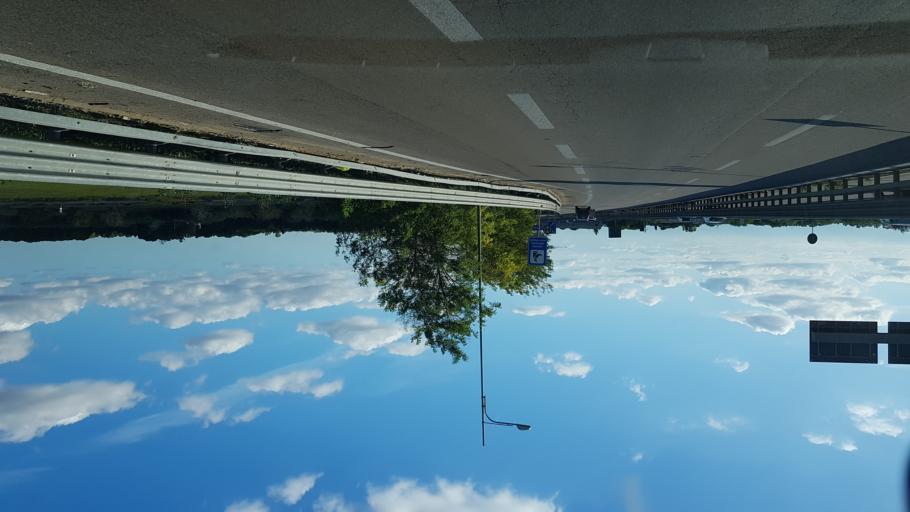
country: IT
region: Apulia
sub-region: Provincia di Lecce
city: Lequile
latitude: 40.3266
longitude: 18.1463
